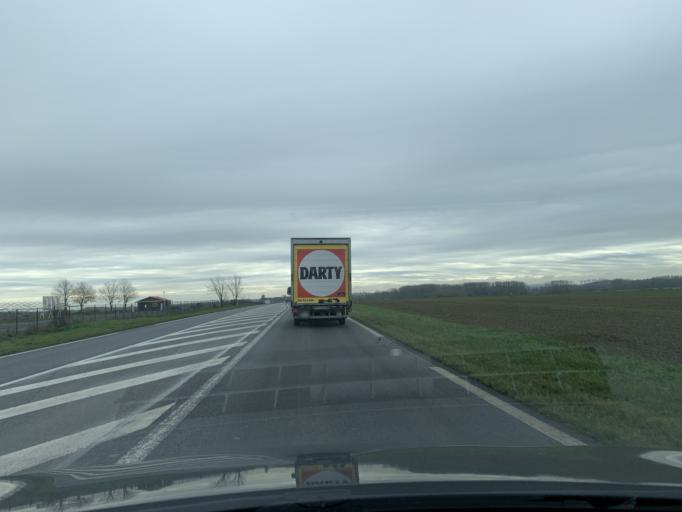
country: FR
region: Nord-Pas-de-Calais
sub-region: Departement du Nord
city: Aubigny-au-Bac
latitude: 50.2829
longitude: 3.1556
